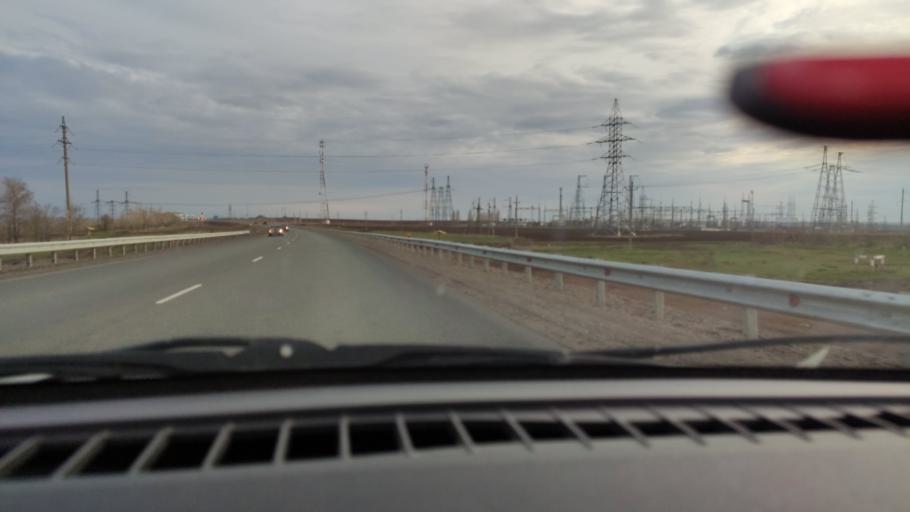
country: RU
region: Orenburg
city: Tatarskaya Kargala
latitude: 51.9834
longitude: 55.1875
